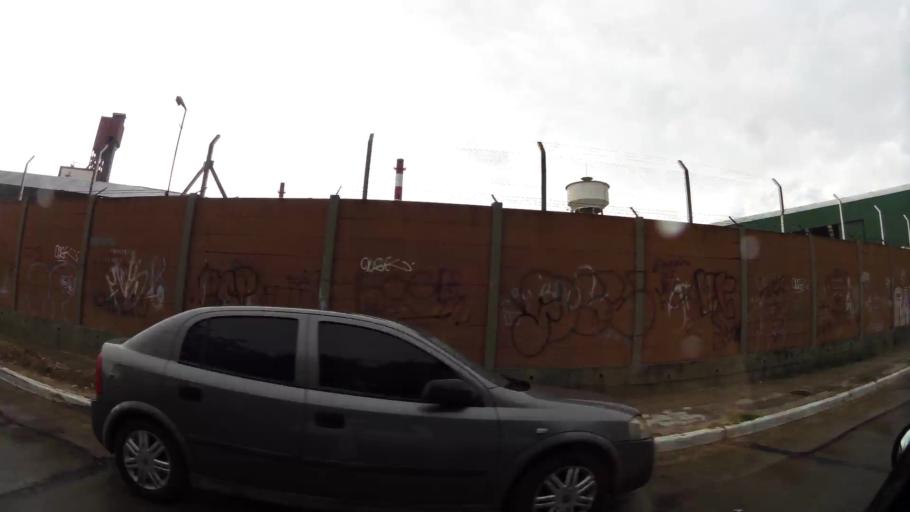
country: AR
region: Buenos Aires
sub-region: Partido de Quilmes
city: Quilmes
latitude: -34.7666
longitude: -58.2097
